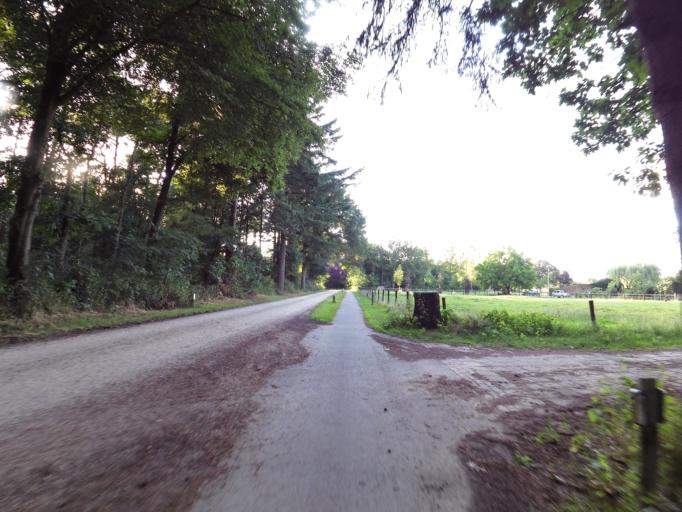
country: NL
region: Gelderland
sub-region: Gemeente Doetinchem
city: Doetinchem
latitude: 51.9925
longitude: 6.2751
